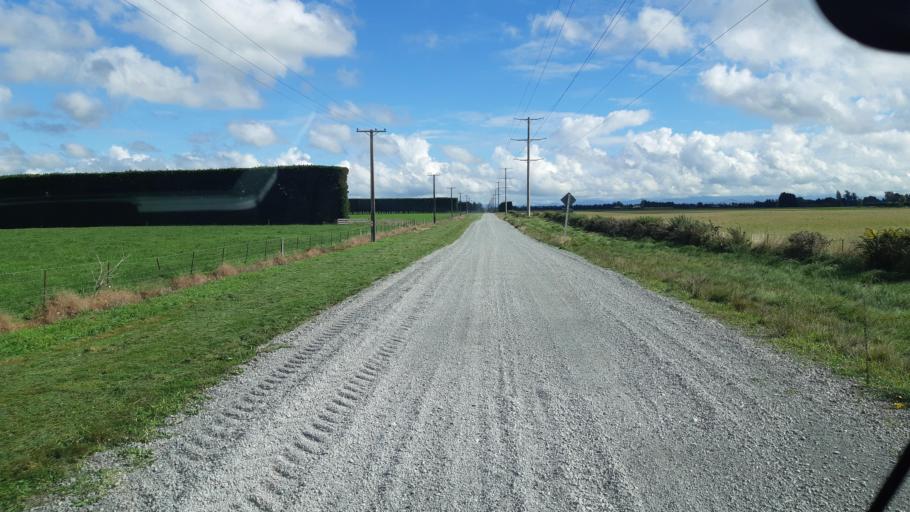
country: NZ
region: Canterbury
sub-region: Selwyn District
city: Darfield
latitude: -43.4728
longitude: 172.2568
